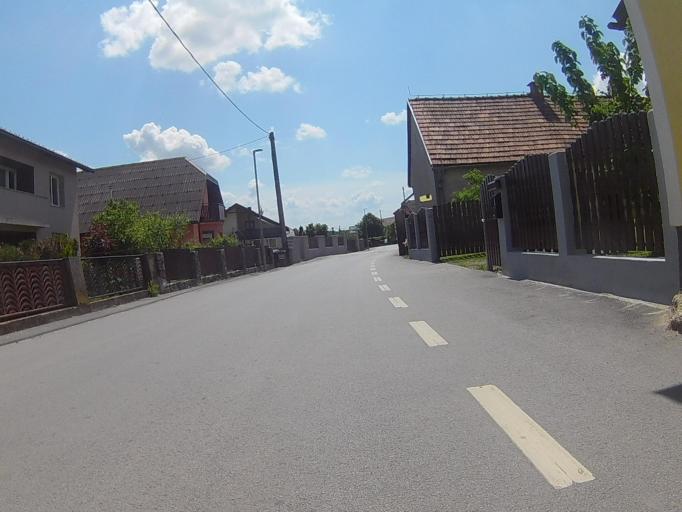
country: SI
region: Hoce-Slivnica
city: Rogoza
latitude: 46.4885
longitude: 15.6938
